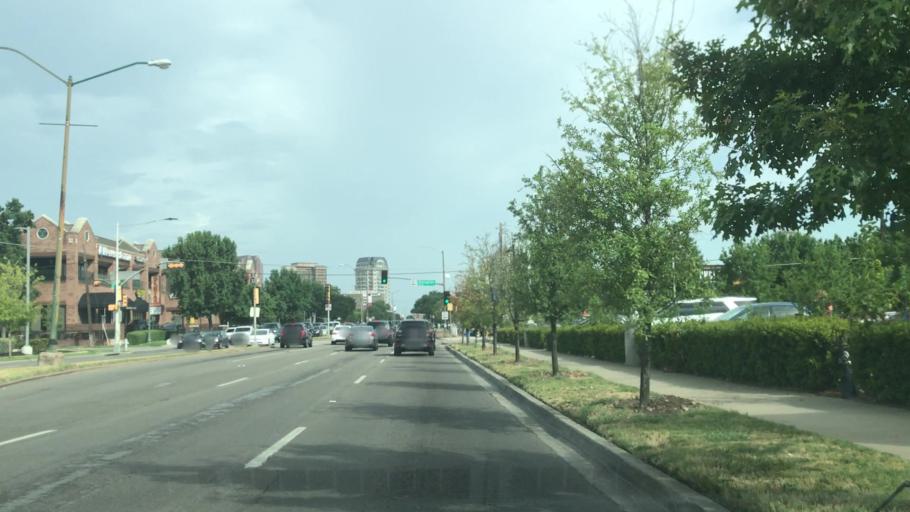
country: US
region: Texas
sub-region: Dallas County
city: Highland Park
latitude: 32.8162
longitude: -96.8107
